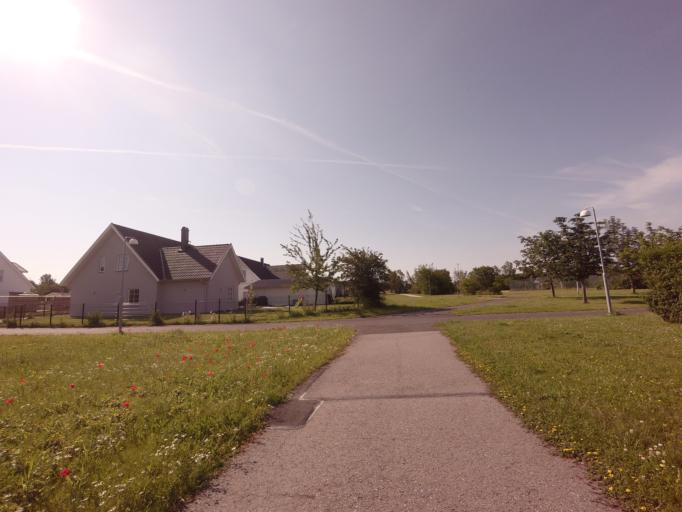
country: SE
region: Skane
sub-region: Malmo
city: Oxie
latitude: 55.4942
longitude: 13.1089
